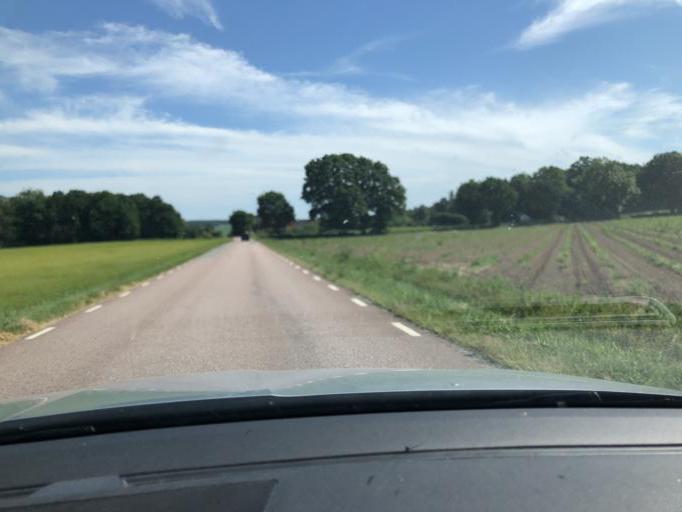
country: SE
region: Blekinge
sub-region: Solvesborgs Kommun
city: Soelvesborg
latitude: 56.1222
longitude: 14.6164
